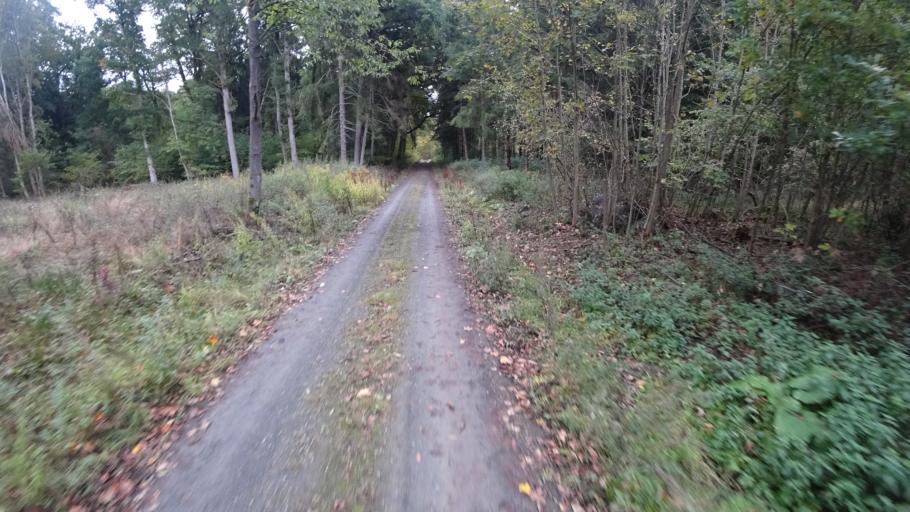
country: DE
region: Rheinland-Pfalz
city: Ruckeroth
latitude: 50.5551
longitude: 7.7628
